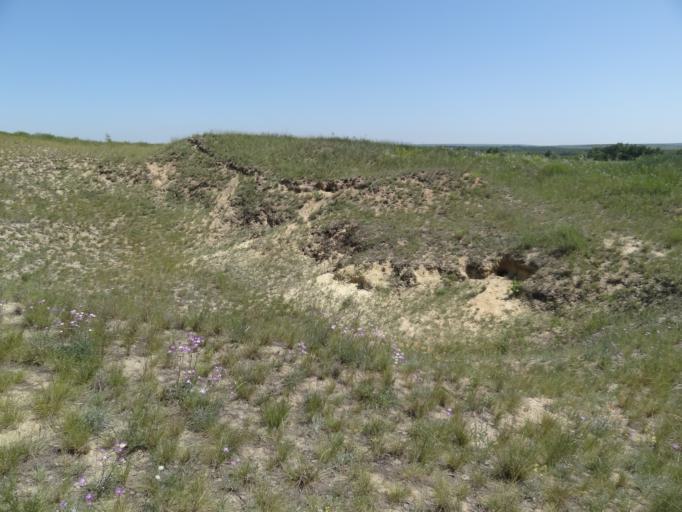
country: RU
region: Saratov
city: Krasnyy Oktyabr'
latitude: 51.2972
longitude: 45.5389
